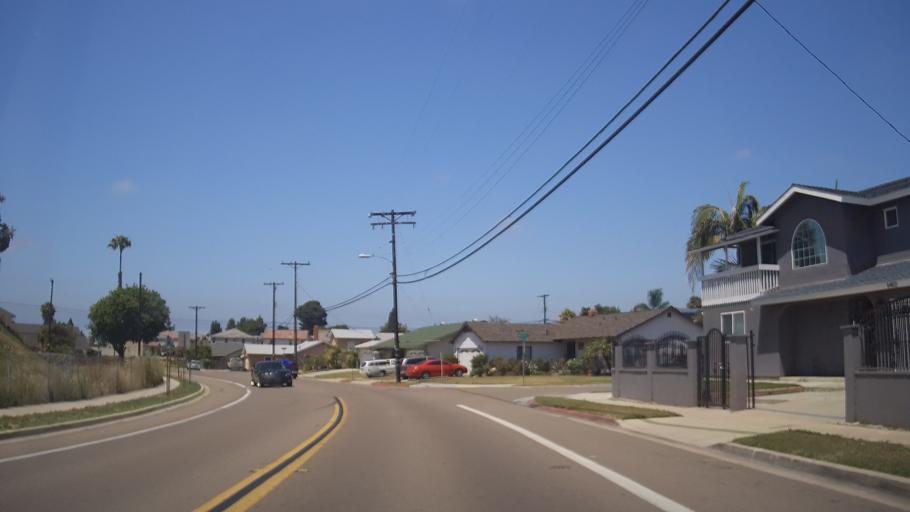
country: US
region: California
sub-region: San Diego County
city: Bonita
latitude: 32.6699
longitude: -117.0489
